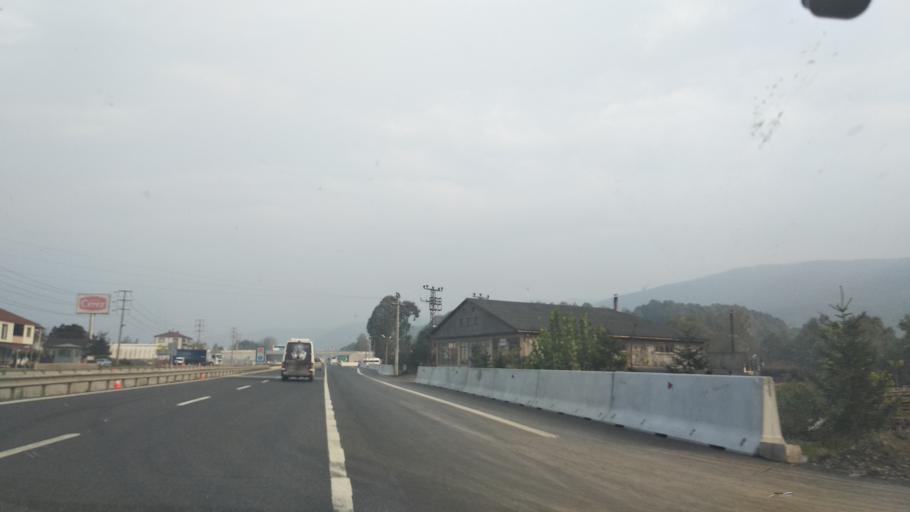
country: TR
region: Duzce
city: Kaynasli
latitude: 40.7836
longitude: 31.2725
